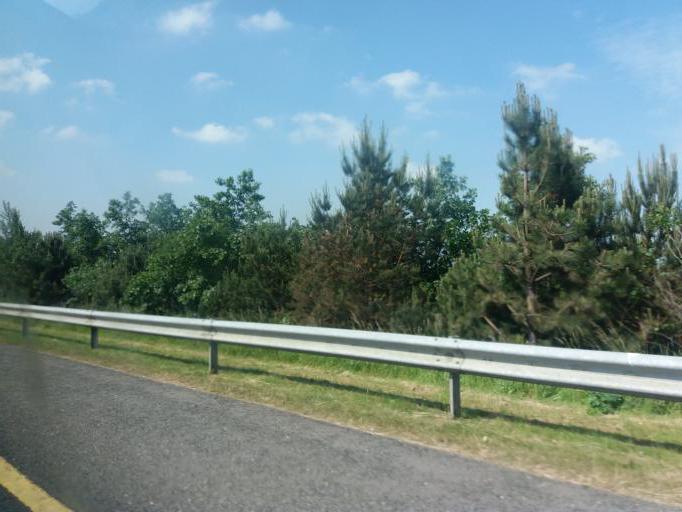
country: IE
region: Leinster
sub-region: An Mhi
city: Ashbourne
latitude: 53.5254
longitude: -6.4179
